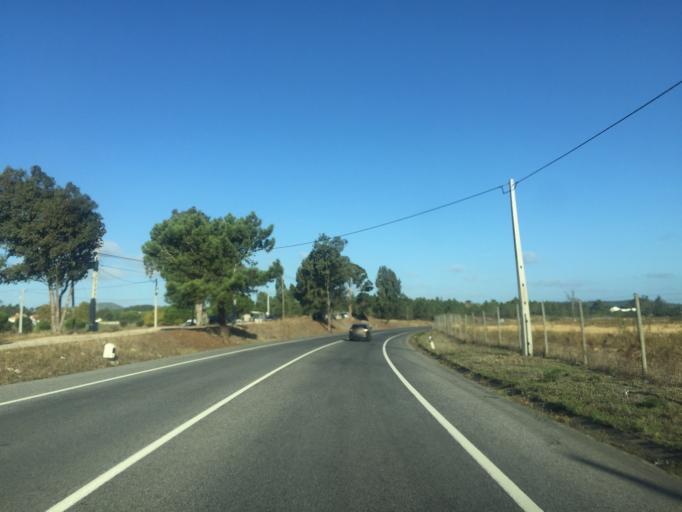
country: PT
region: Lisbon
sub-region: Azambuja
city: Alcoentre
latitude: 39.1922
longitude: -8.9511
